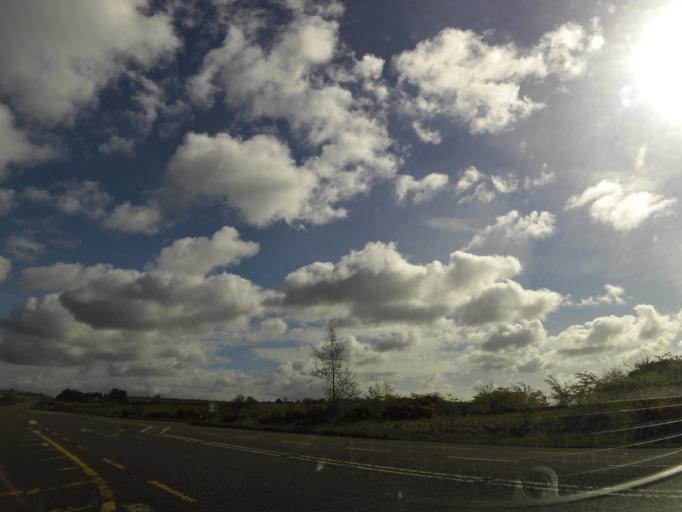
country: IE
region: Connaught
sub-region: Maigh Eo
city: Claremorris
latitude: 53.7788
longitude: -8.9487
